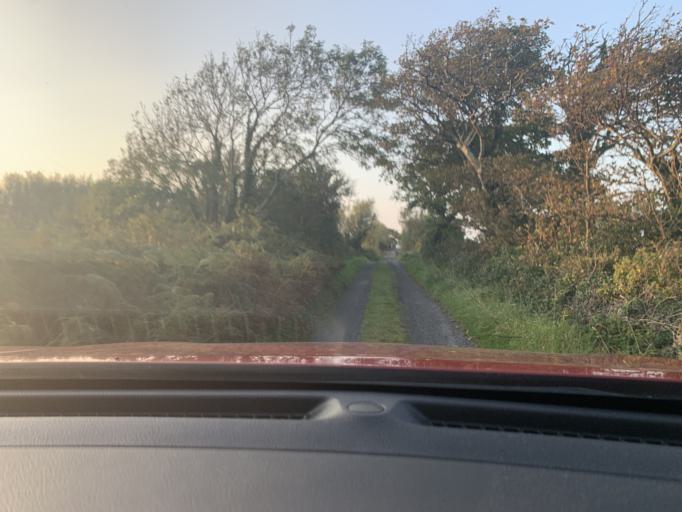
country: IE
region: Connaught
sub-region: County Leitrim
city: Kinlough
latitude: 54.4569
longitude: -8.3988
